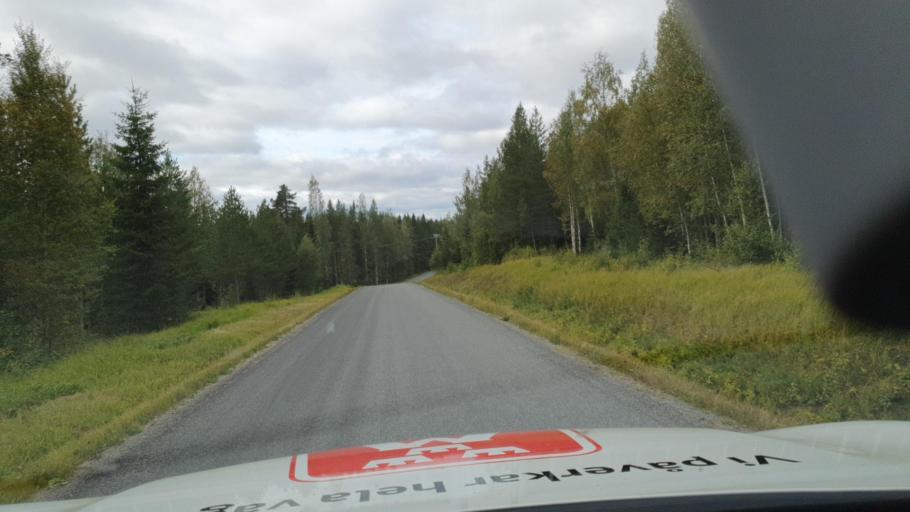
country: SE
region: Jaemtland
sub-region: OEstersunds Kommun
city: Ostersund
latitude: 63.1440
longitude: 14.5543
